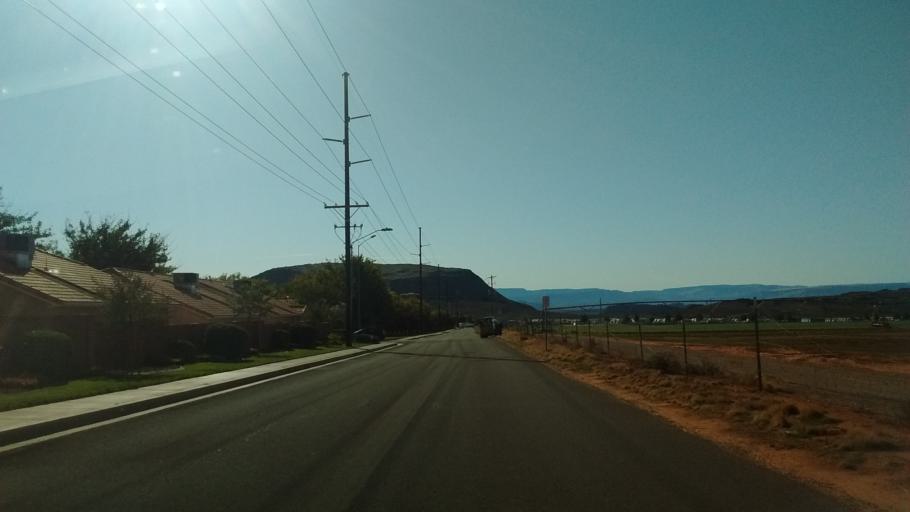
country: US
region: Utah
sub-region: Washington County
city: Washington
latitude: 37.1358
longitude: -113.4910
